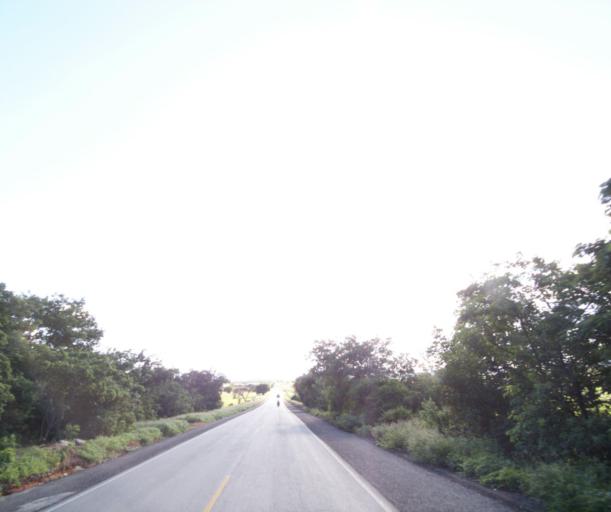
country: BR
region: Bahia
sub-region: Guanambi
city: Guanambi
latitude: -14.1552
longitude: -42.7036
